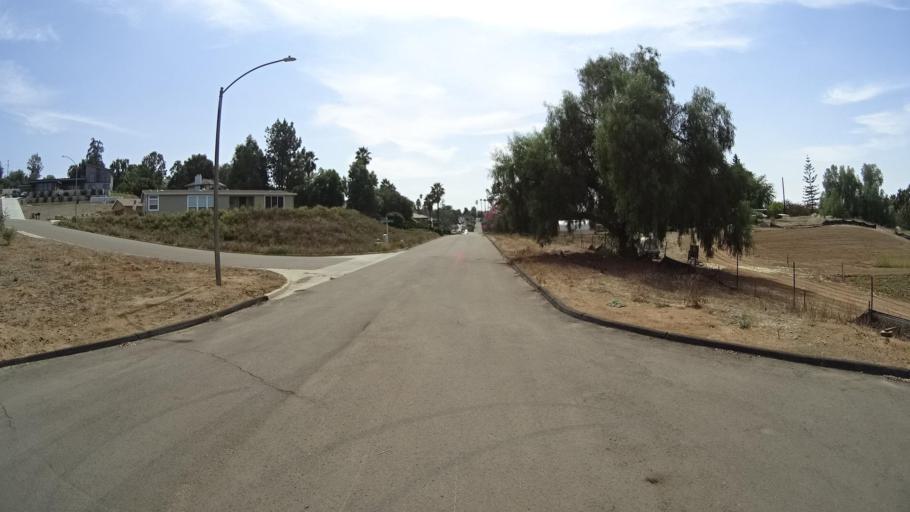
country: US
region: California
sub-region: San Diego County
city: Escondido
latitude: 33.1161
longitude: -117.0394
